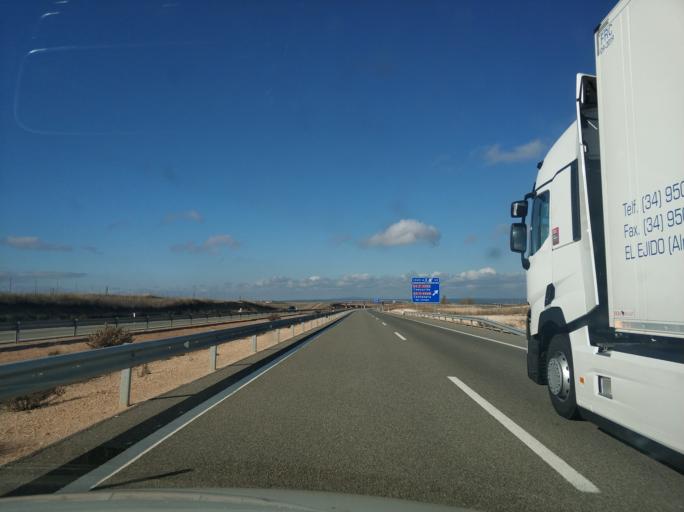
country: ES
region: Castille and Leon
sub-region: Provincia de Soria
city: Coscurita
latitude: 41.4067
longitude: -2.4813
